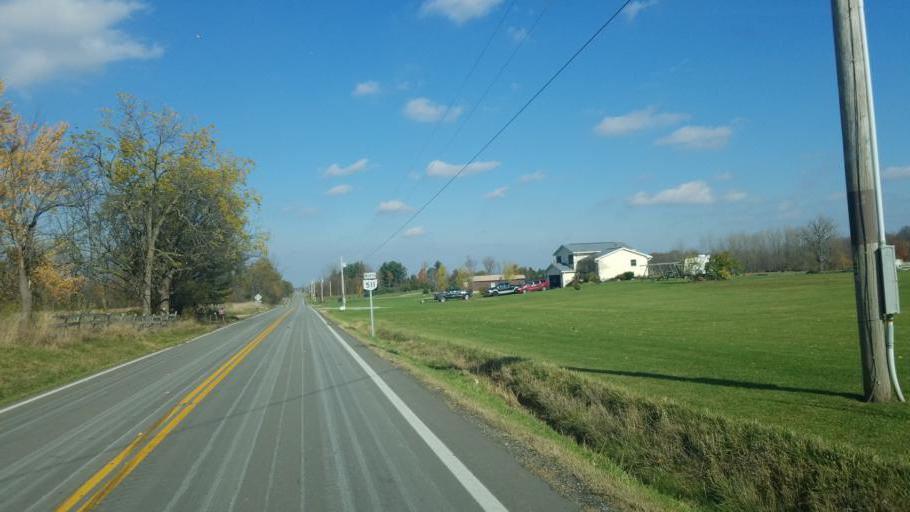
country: US
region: Ohio
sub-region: Huron County
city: New London
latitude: 41.0583
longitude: -82.3043
